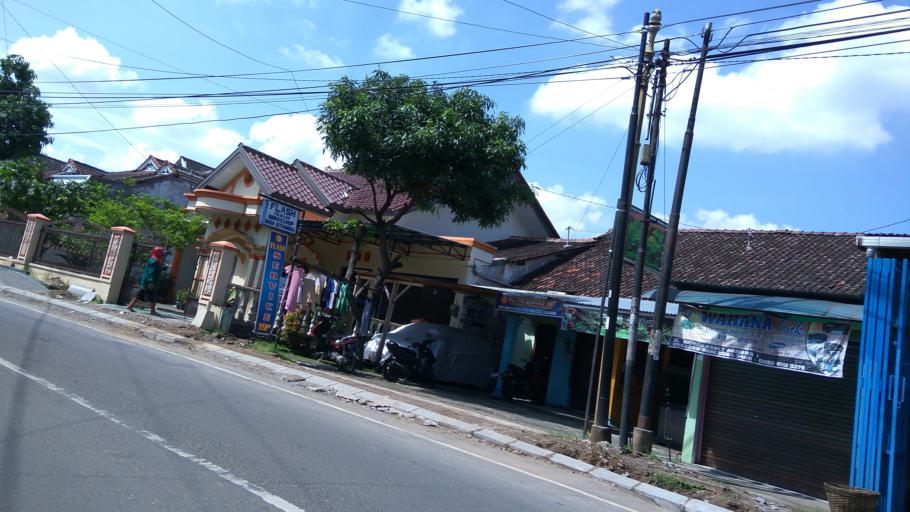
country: ID
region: Central Java
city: Ungaran
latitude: -7.1302
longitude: 110.4089
